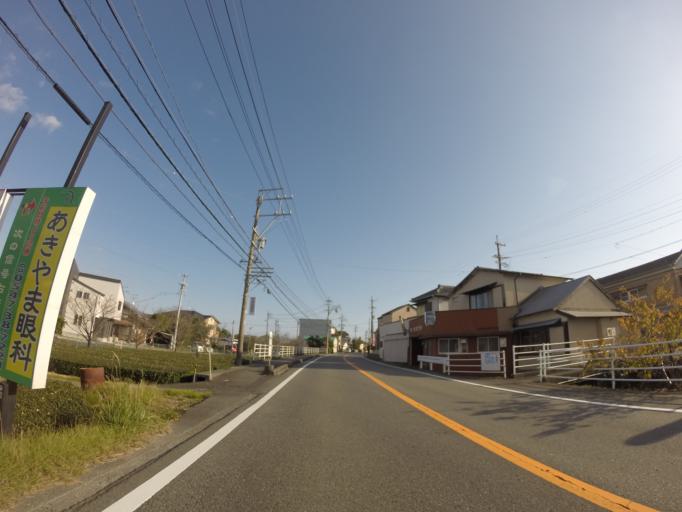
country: JP
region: Shizuoka
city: Shimada
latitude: 34.8104
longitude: 138.2177
